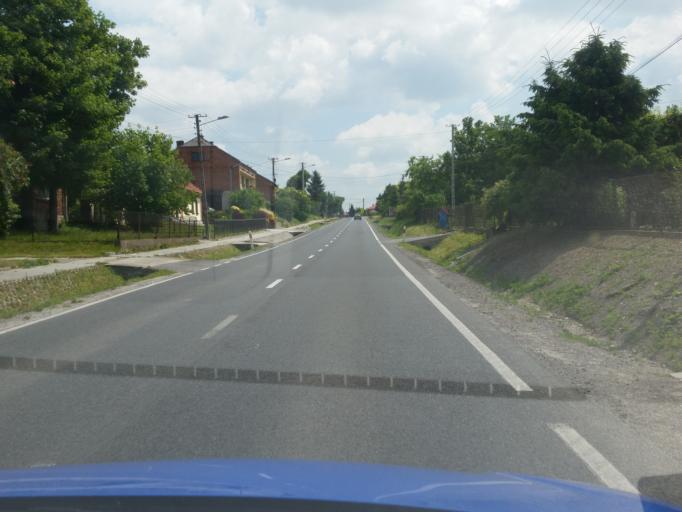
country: PL
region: Lesser Poland Voivodeship
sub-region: Powiat miechowski
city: Miechow
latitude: 50.3576
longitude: 20.0761
